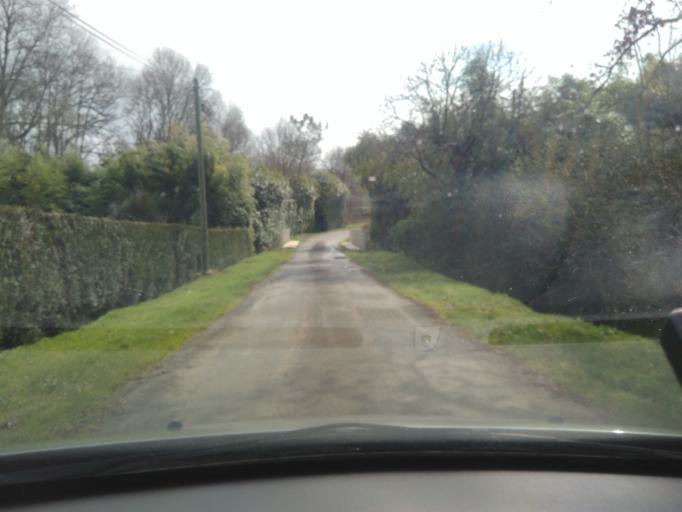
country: FR
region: Pays de la Loire
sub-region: Departement de la Vendee
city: Sainte-Cecile
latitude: 46.7014
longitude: -1.1263
